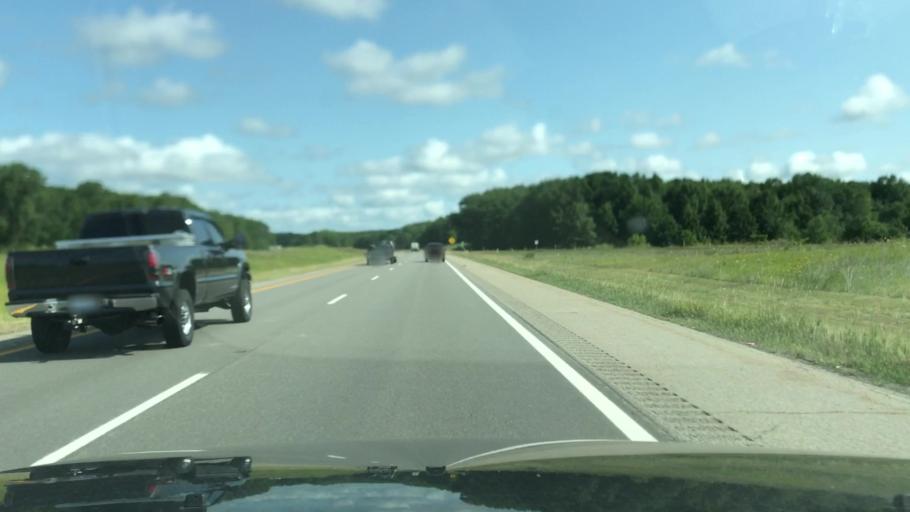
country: US
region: Michigan
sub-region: Montcalm County
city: Howard City
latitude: 43.3396
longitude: -85.5111
